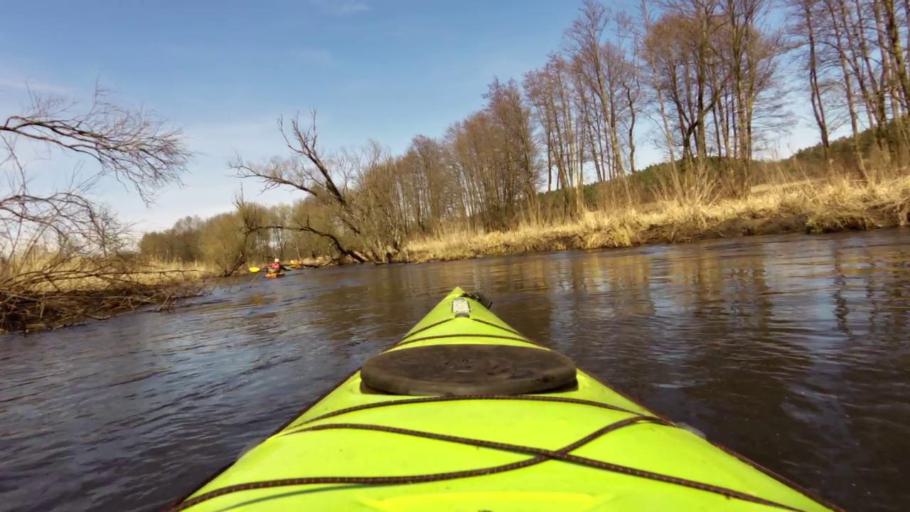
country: PL
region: West Pomeranian Voivodeship
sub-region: Powiat lobeski
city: Lobez
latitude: 53.6656
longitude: 15.5657
